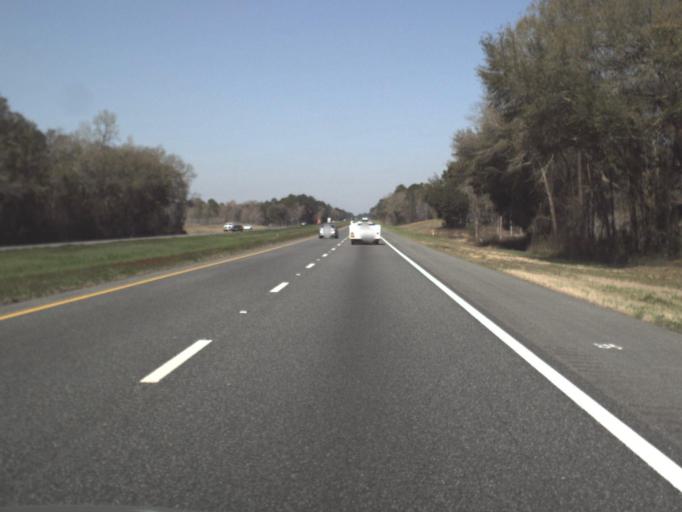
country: US
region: Florida
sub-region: Jackson County
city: Marianna
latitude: 30.6961
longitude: -85.1273
